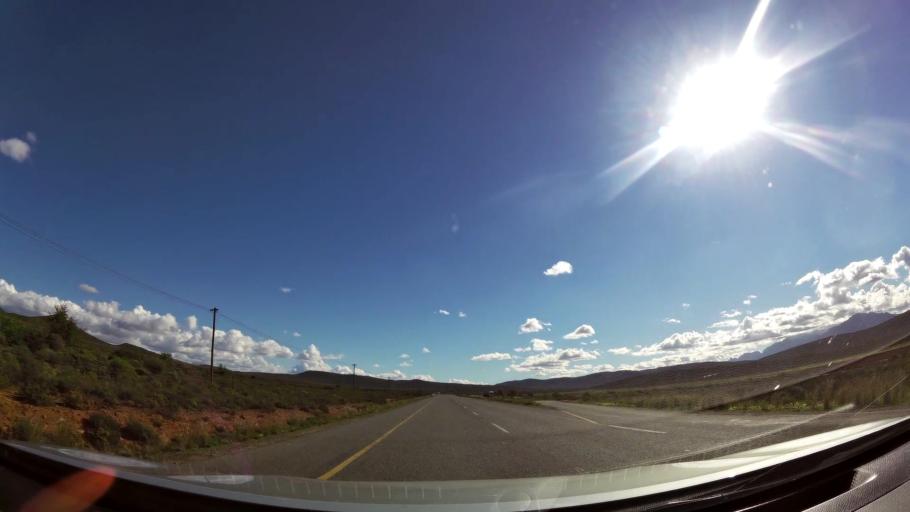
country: ZA
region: Western Cape
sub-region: Cape Winelands District Municipality
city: Worcester
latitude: -33.7517
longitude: 19.7205
